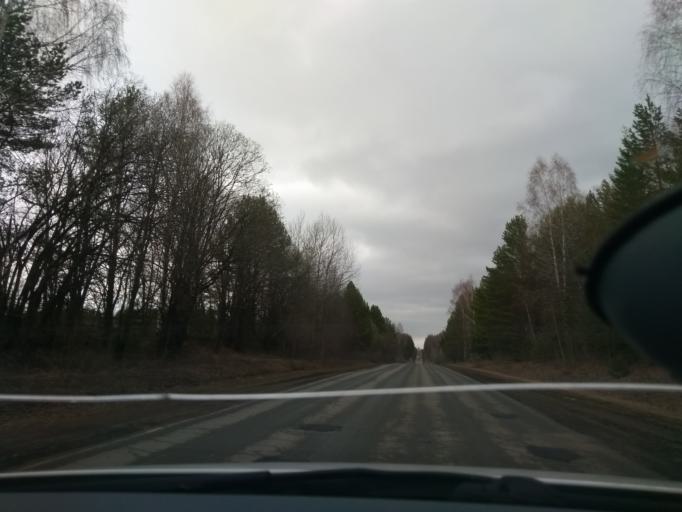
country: RU
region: Perm
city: Kungur
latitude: 57.3524
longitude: 56.8022
